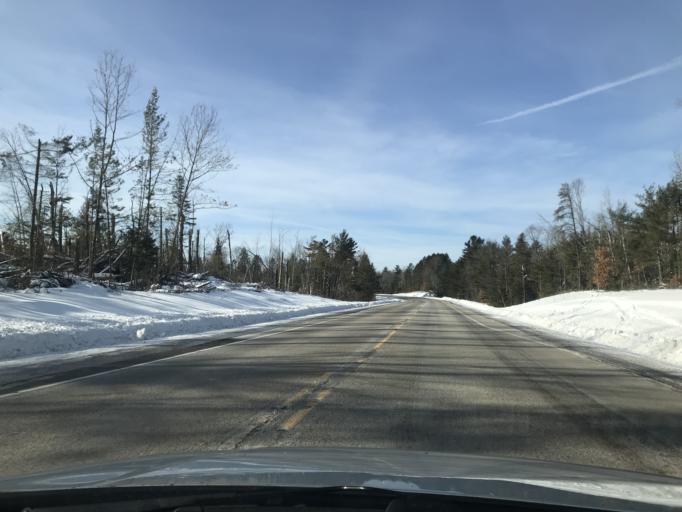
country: US
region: Wisconsin
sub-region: Oconto County
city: Gillett
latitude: 45.1265
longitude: -88.4026
